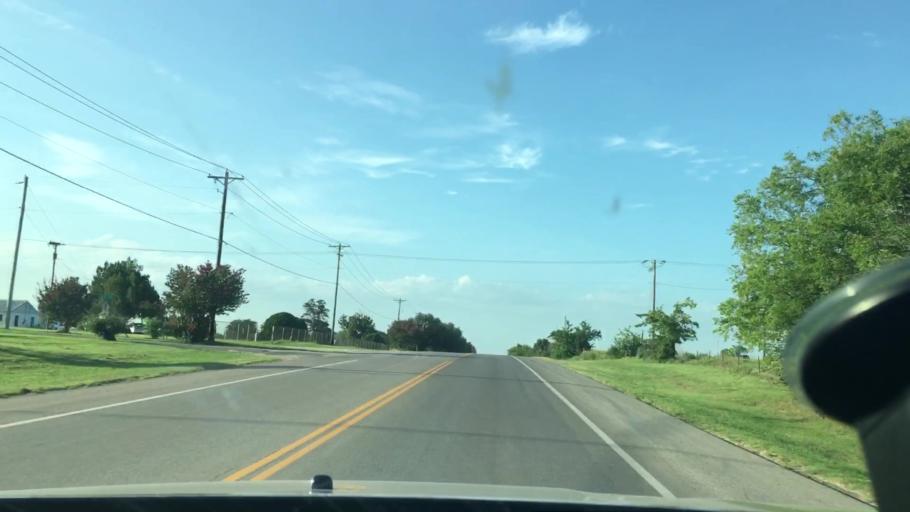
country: US
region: Oklahoma
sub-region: Garvin County
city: Pauls Valley
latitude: 34.7158
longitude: -97.2130
